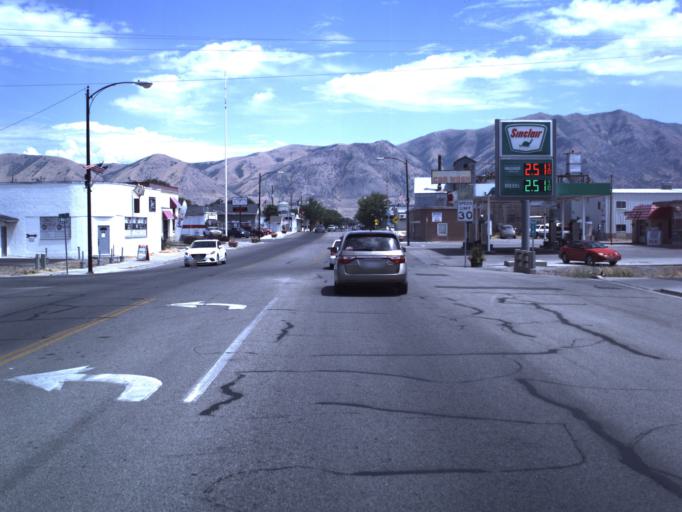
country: US
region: Utah
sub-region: Box Elder County
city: Tremonton
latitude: 41.7116
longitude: -112.1718
